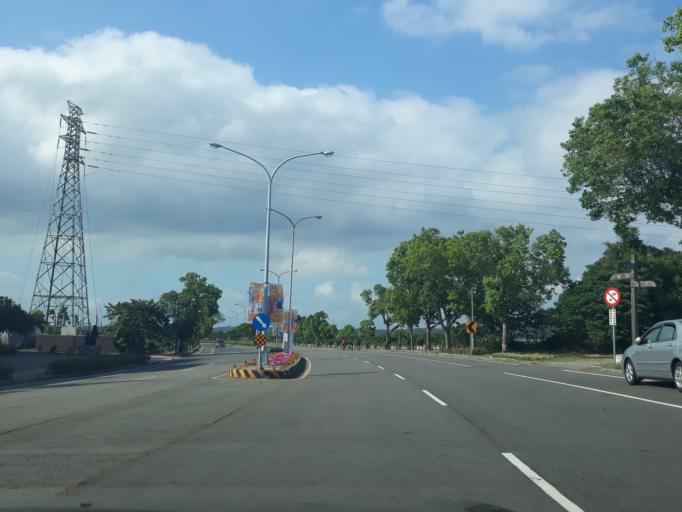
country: TW
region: Taiwan
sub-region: Miaoli
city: Miaoli
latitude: 24.5815
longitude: 120.8432
